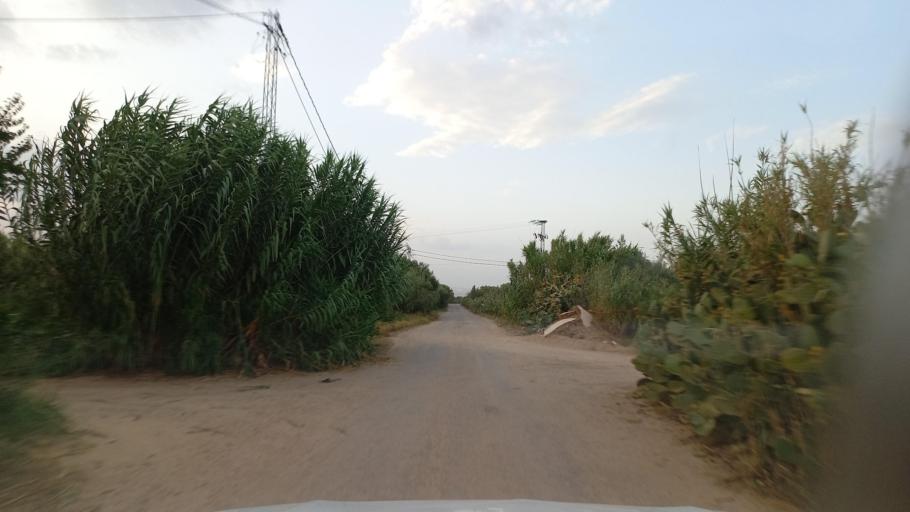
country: TN
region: Al Qasrayn
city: Kasserine
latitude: 35.2779
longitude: 9.0514
